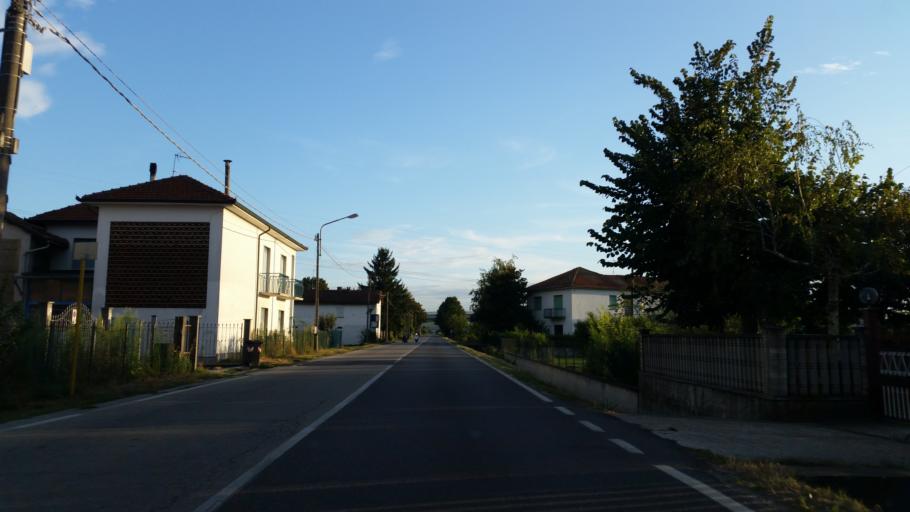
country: IT
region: Piedmont
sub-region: Provincia di Asti
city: Mongardino
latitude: 44.8582
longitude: 8.2022
